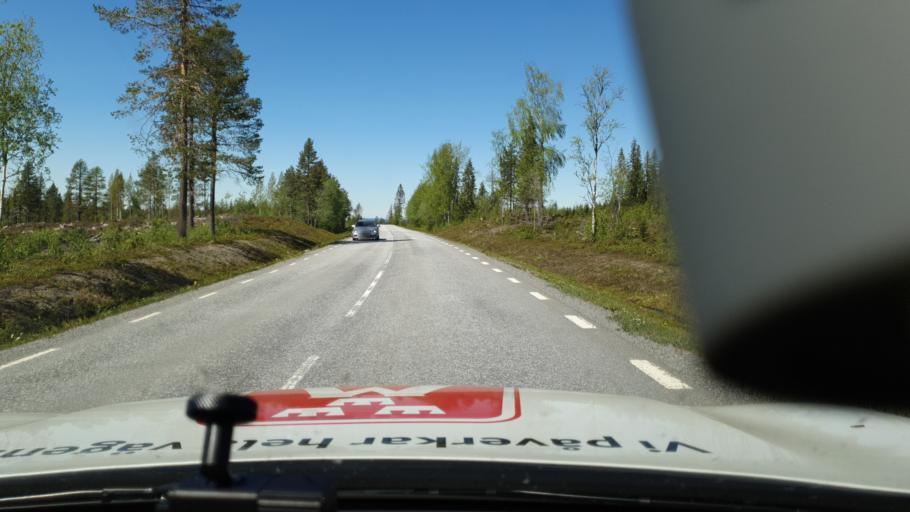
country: SE
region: Vaesterbotten
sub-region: Storumans Kommun
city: Storuman
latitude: 65.1401
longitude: 17.1010
